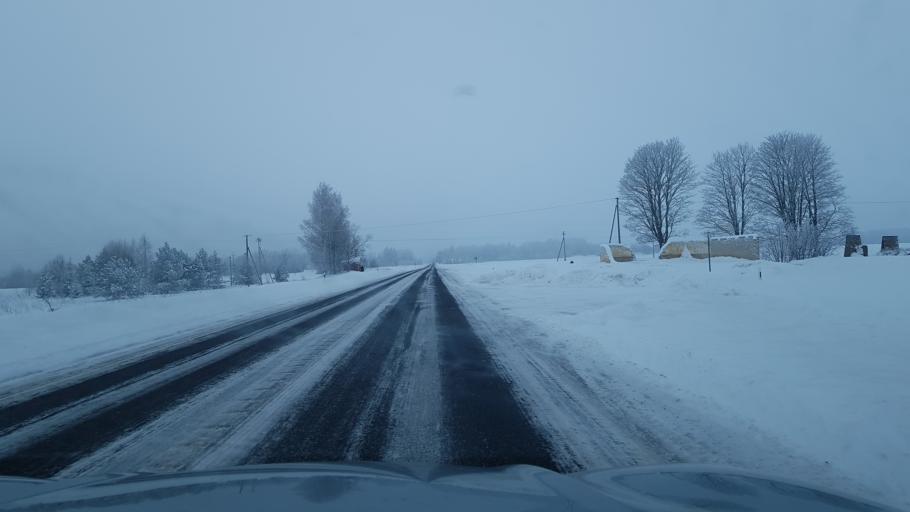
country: EE
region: Ida-Virumaa
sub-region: Johvi vald
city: Johvi
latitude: 59.2425
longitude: 27.3607
